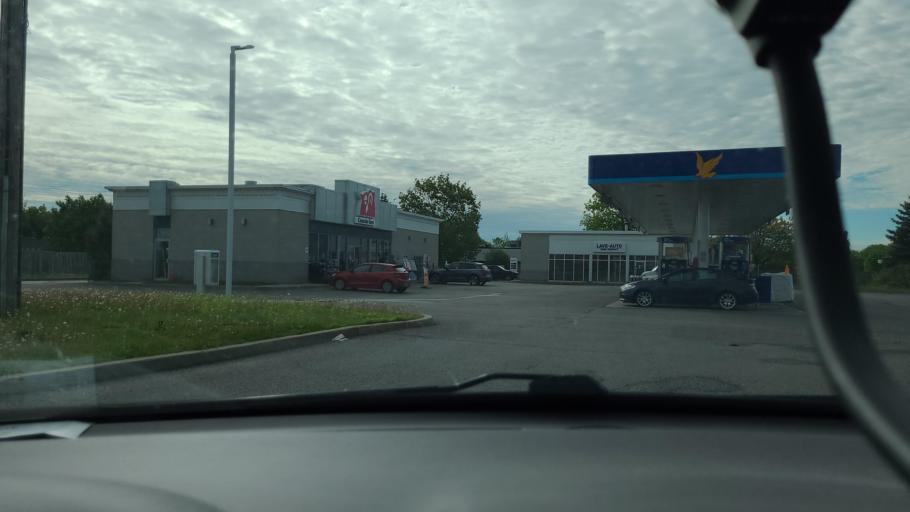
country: CA
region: Quebec
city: L'Ancienne-Lorette
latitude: 46.7649
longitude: -71.3703
